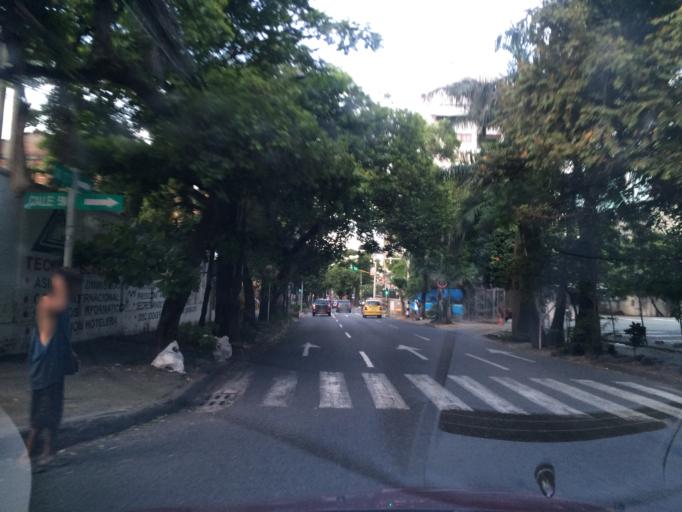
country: CO
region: Valle del Cauca
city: Cali
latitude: 3.4524
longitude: -76.5384
